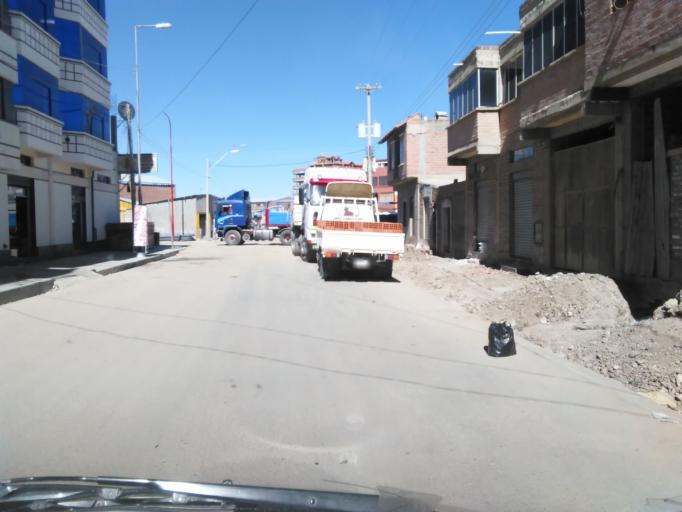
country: BO
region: Oruro
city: Oruro
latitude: -17.9700
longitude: -67.0950
